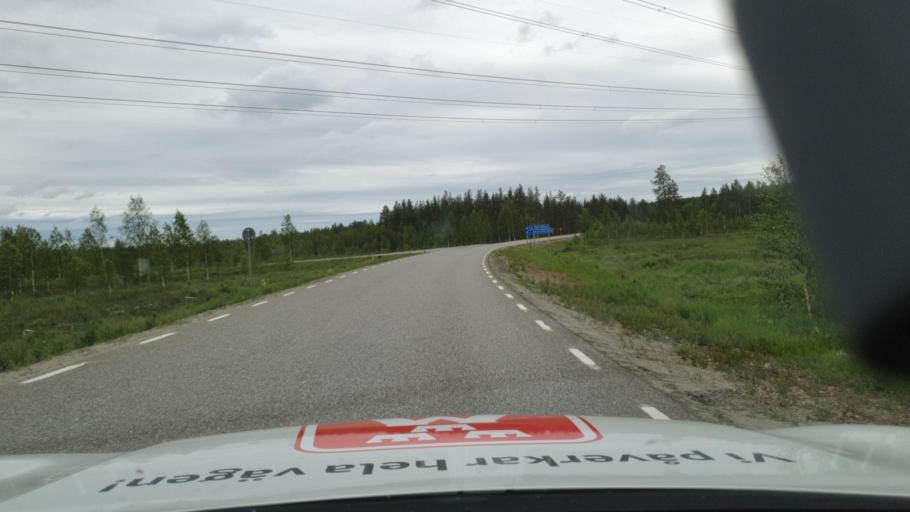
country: SE
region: Vaesterbotten
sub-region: Lycksele Kommun
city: Lycksele
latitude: 64.1637
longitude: 18.3589
